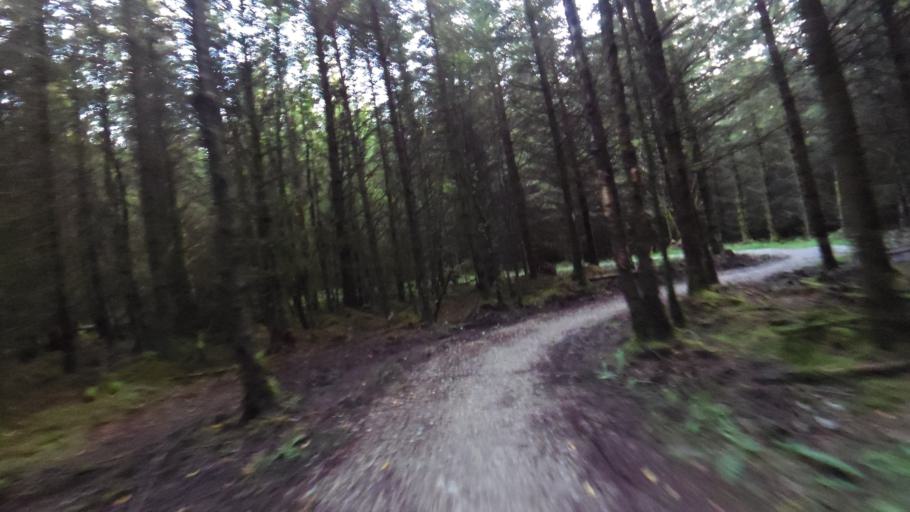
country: GB
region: England
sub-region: Lancashire
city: Clitheroe
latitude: 53.9953
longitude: -2.3860
